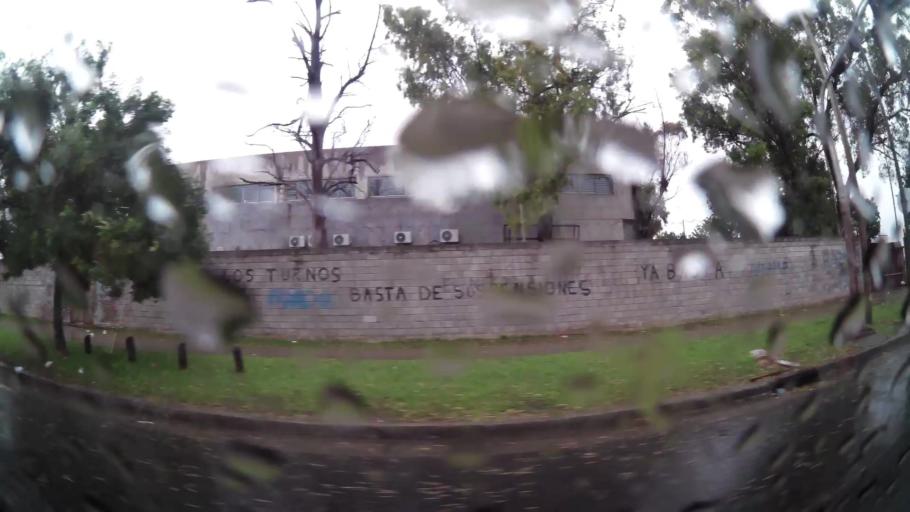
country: AR
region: Buenos Aires F.D.
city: Villa Lugano
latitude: -34.6550
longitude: -58.4379
